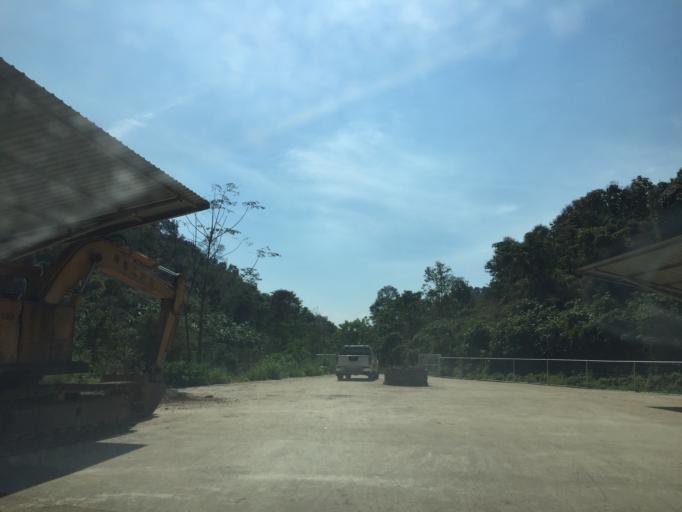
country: TH
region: Chiang Mai
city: Samoeng
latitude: 19.0114
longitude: 98.7314
